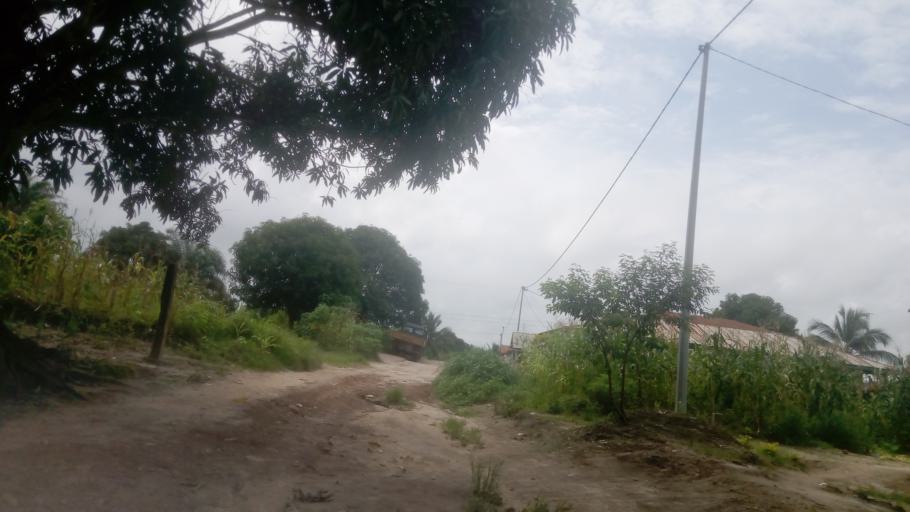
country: SL
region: Northern Province
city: Lunsar
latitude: 8.6908
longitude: -12.5395
